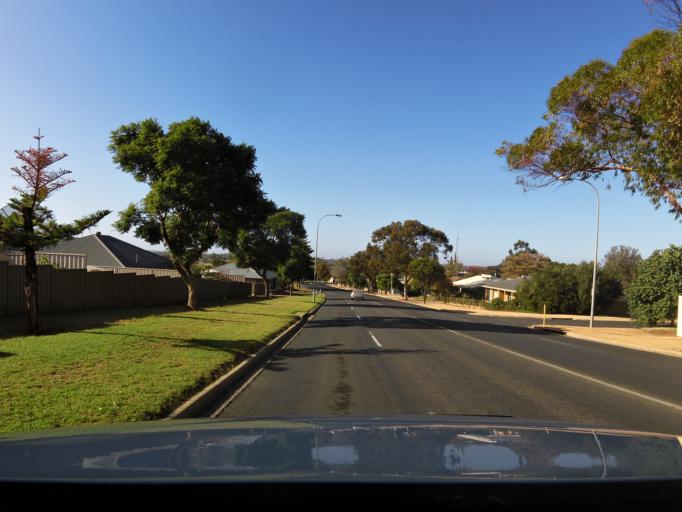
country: AU
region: South Australia
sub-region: Berri and Barmera
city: Berri
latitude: -34.2740
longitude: 140.6081
